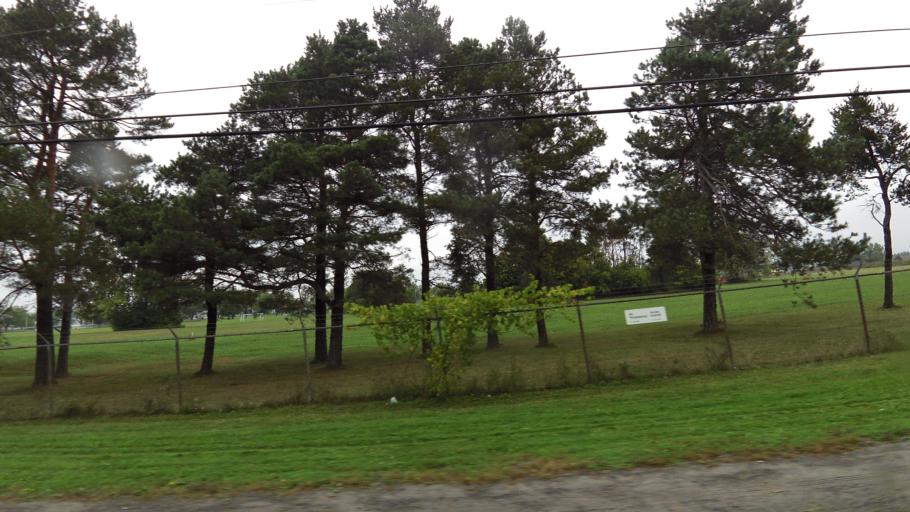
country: CA
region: Ontario
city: Kingston
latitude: 44.2408
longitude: -76.4447
